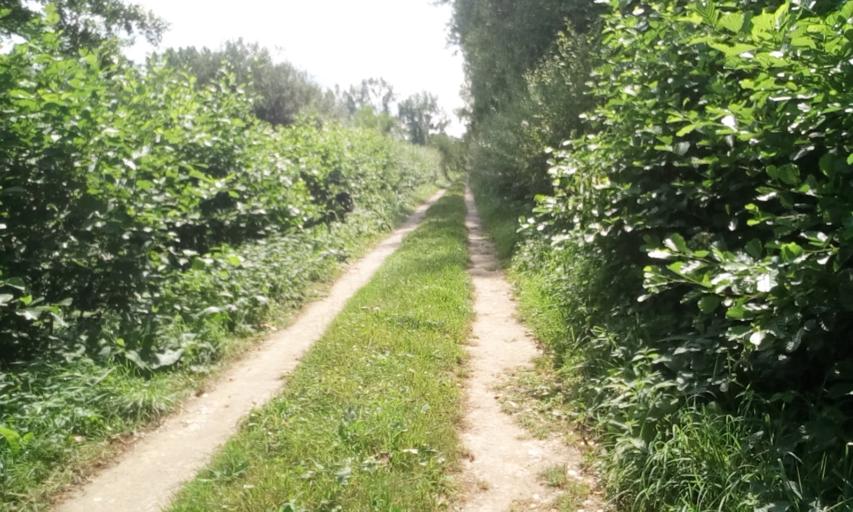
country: FR
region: Lower Normandy
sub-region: Departement du Calvados
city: Bavent
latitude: 49.2362
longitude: -0.1645
